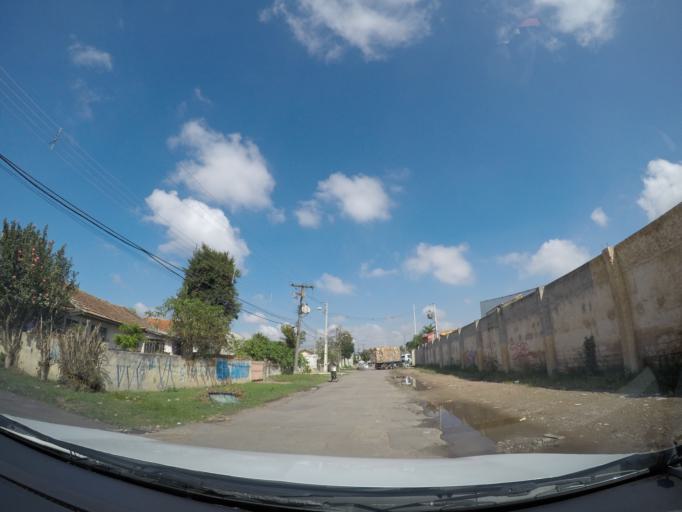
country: BR
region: Parana
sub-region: Sao Jose Dos Pinhais
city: Sao Jose dos Pinhais
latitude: -25.4980
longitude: -49.2204
